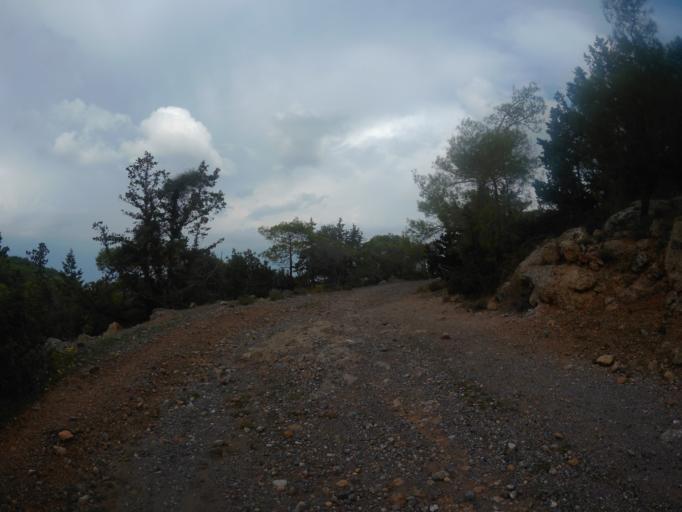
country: CY
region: Ammochostos
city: Lefkonoiko
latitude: 35.3232
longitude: 33.6206
